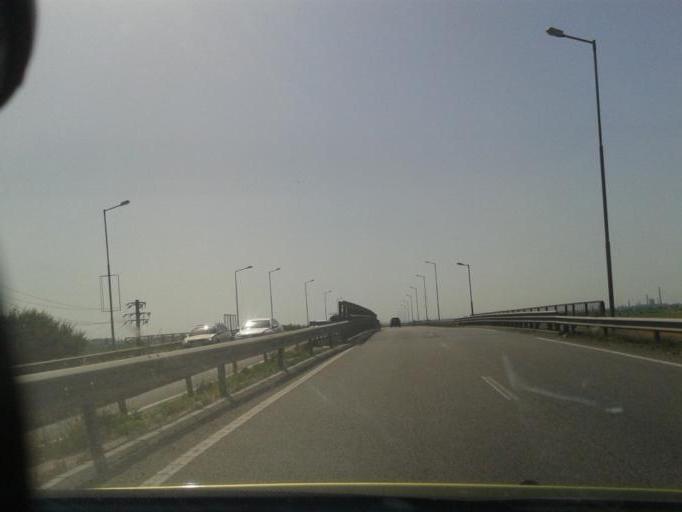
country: RO
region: Prahova
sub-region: Comuna Targsoru Vechi
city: Strejnicu
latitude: 44.9322
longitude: 25.9677
